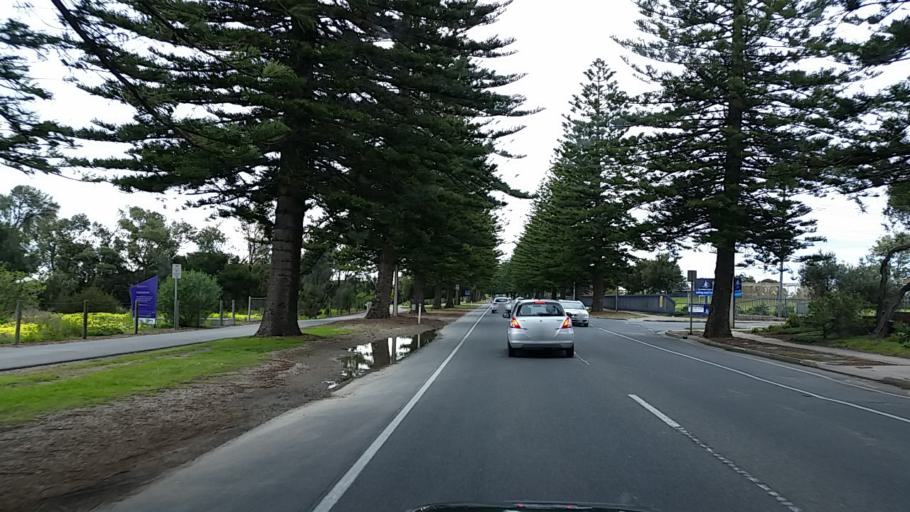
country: AU
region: South Australia
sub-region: Port Adelaide Enfield
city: Birkenhead
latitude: -34.8048
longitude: 138.4915
